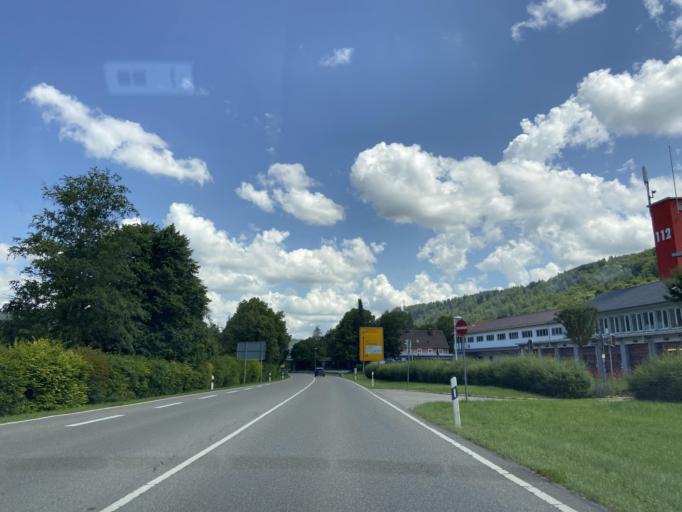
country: DE
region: Baden-Wuerttemberg
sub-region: Tuebingen Region
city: Albstadt
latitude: 48.2092
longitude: 9.0168
